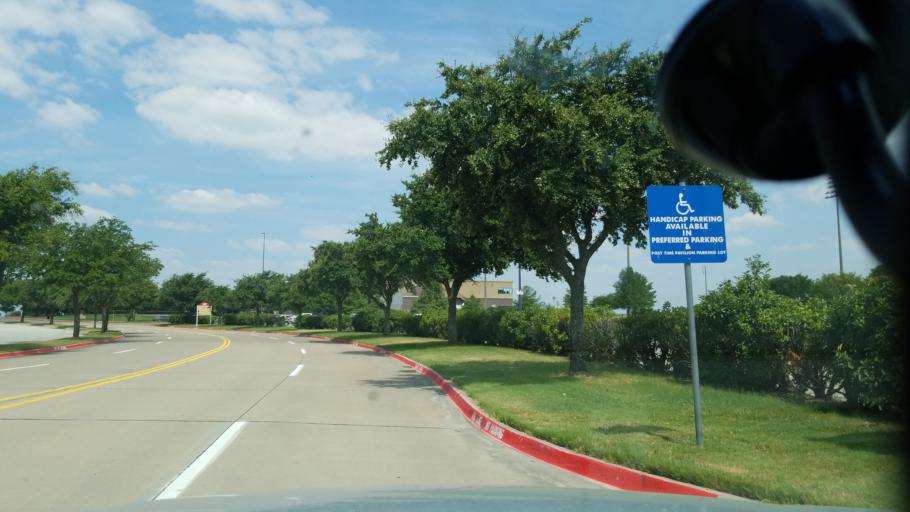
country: US
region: Texas
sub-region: Dallas County
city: Grand Prairie
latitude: 32.7712
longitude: -96.9856
